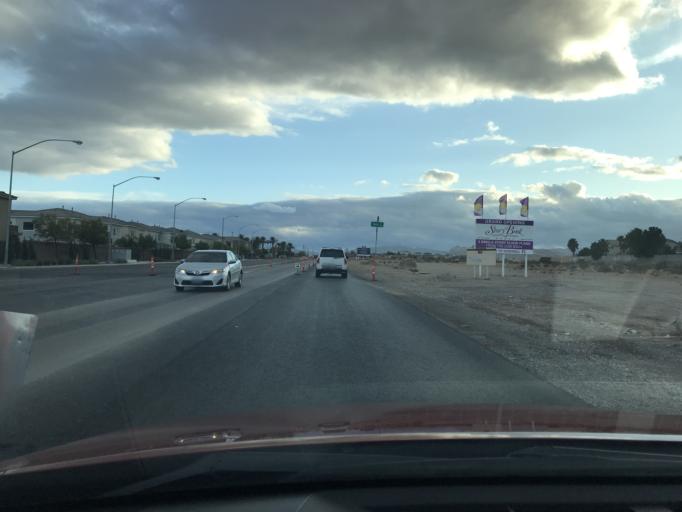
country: US
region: Nevada
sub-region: Clark County
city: Enterprise
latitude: 36.0392
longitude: -115.2791
